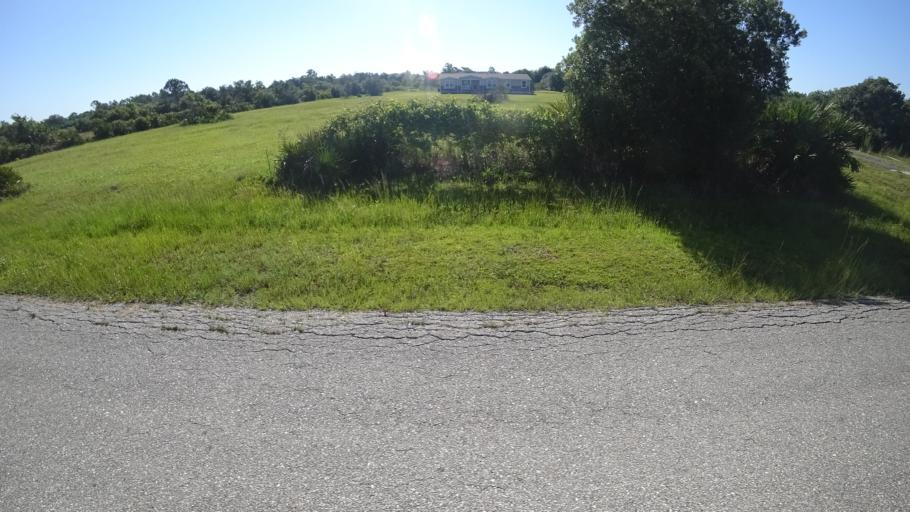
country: US
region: Florida
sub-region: Sarasota County
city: The Meadows
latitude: 27.4117
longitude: -82.3121
